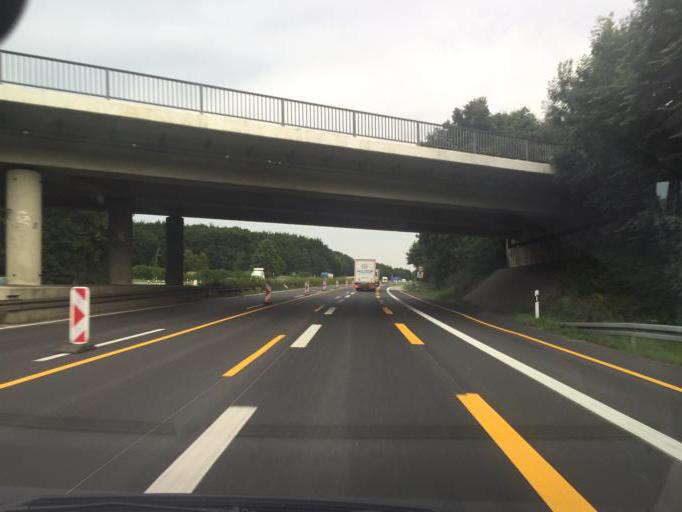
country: DE
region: North Rhine-Westphalia
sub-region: Regierungsbezirk Dusseldorf
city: Viersen
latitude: 51.2731
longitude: 6.3490
